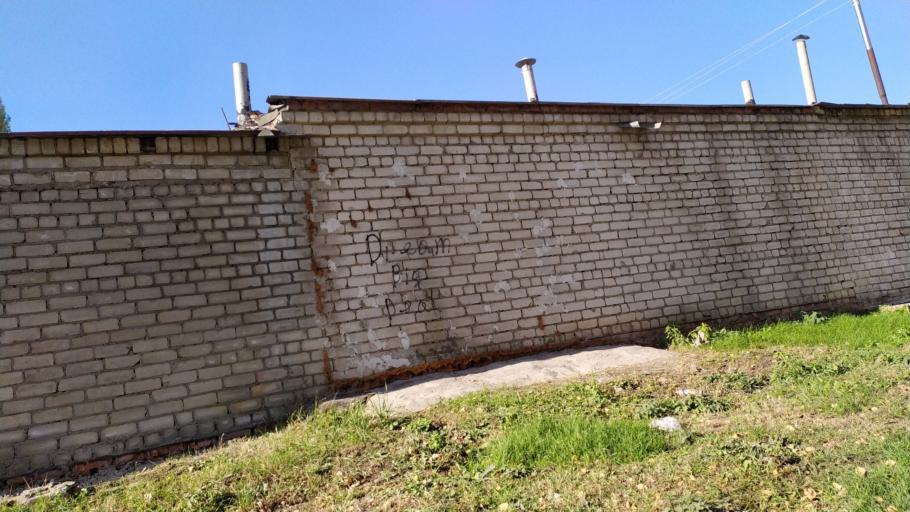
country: RU
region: Kursk
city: Kursk
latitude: 51.6521
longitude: 36.1532
